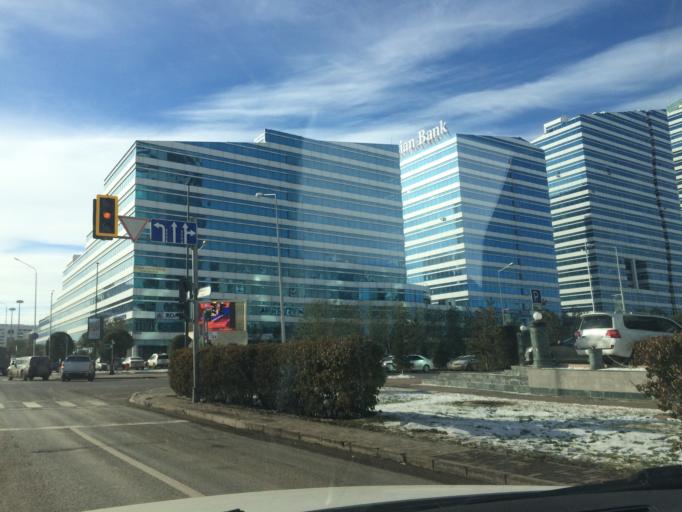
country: KZ
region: Astana Qalasy
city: Astana
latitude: 51.1312
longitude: 71.4298
